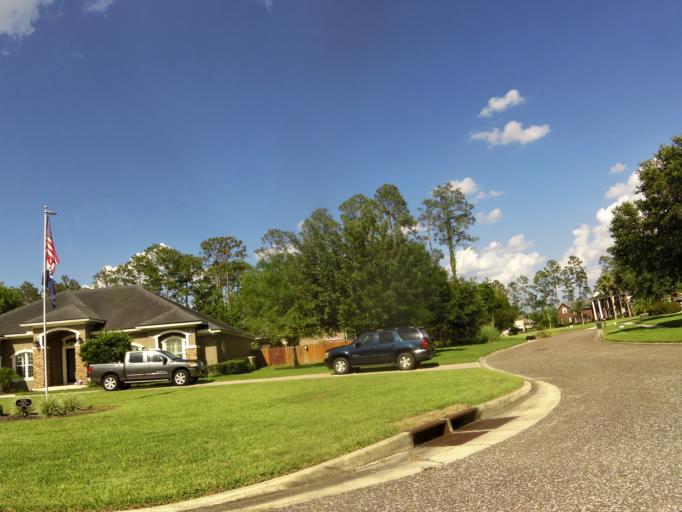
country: US
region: Florida
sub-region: Saint Johns County
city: Fruit Cove
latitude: 30.0644
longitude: -81.6507
